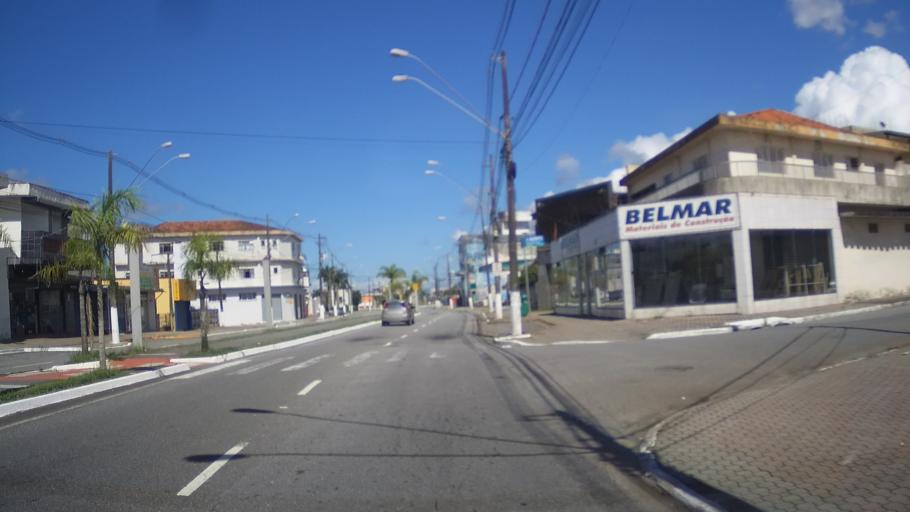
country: BR
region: Sao Paulo
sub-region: Praia Grande
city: Praia Grande
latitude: -24.0351
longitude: -46.5039
